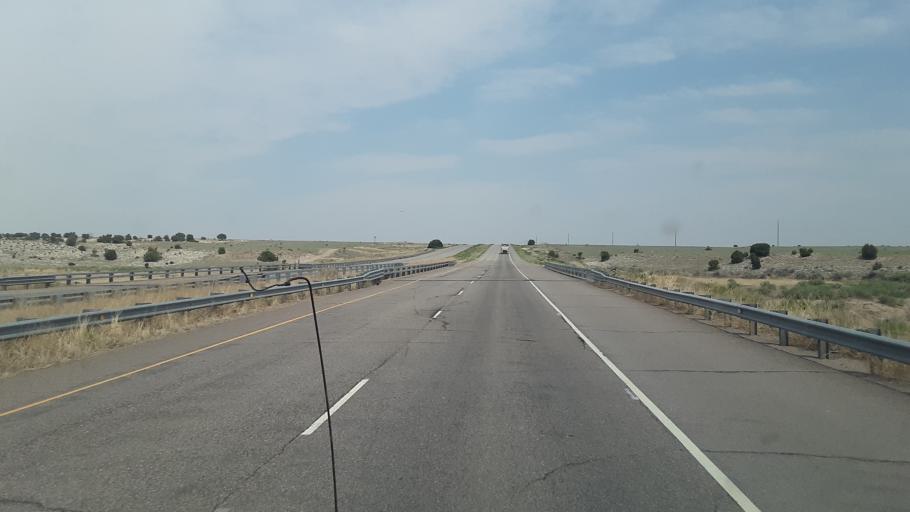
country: US
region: Colorado
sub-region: Pueblo County
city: Pueblo West
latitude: 38.3540
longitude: -104.8350
